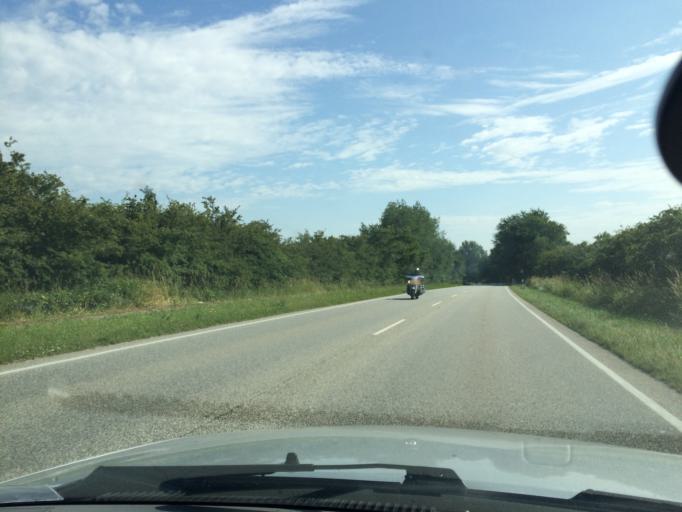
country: DE
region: Schleswig-Holstein
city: Sankelmark
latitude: 54.7310
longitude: 9.4418
